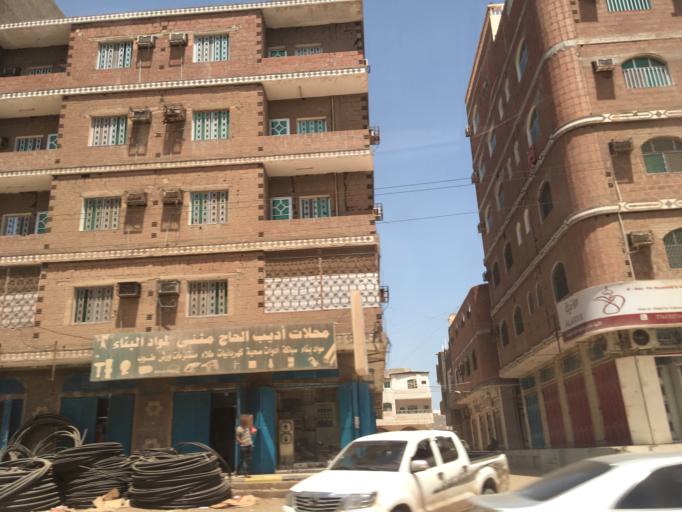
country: YE
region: Aden
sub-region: Al Mansura
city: Al Mansurah
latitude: 12.8635
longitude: 44.9717
